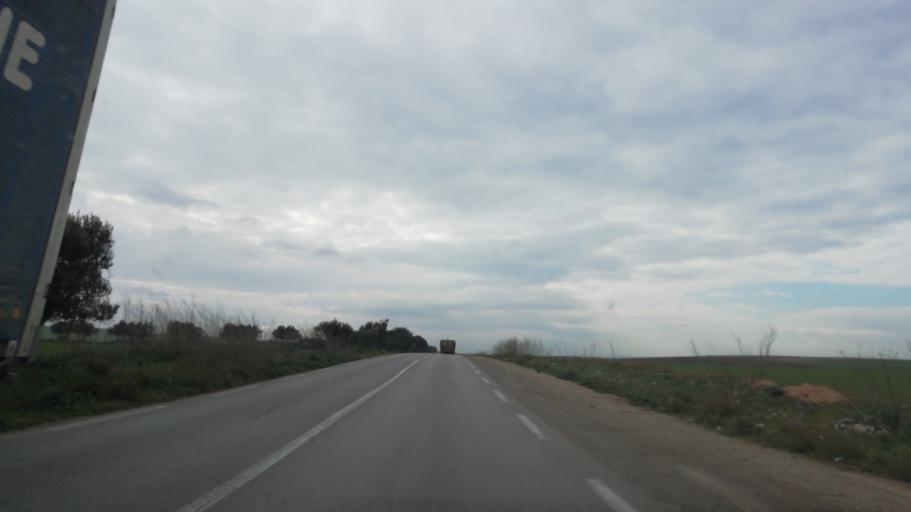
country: DZ
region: Oran
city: Ain el Bya
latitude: 35.7637
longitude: -0.3491
